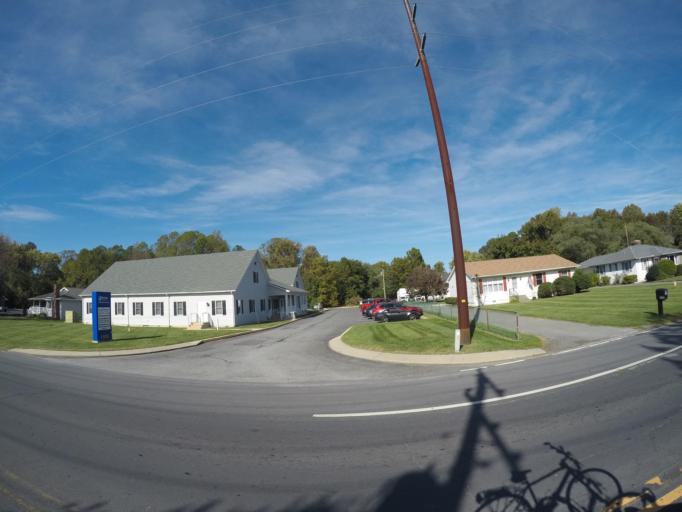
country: US
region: Delaware
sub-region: Sussex County
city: Lewes
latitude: 38.7604
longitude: -75.1539
